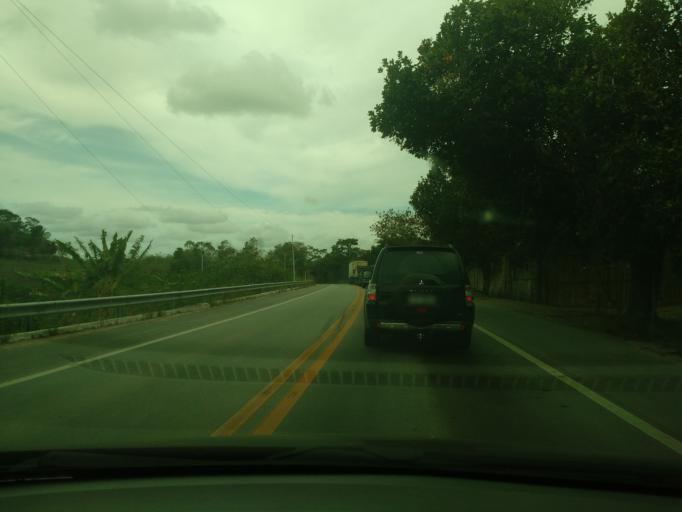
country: BR
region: Alagoas
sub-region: Messias
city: Messias
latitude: -9.3687
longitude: -35.8468
